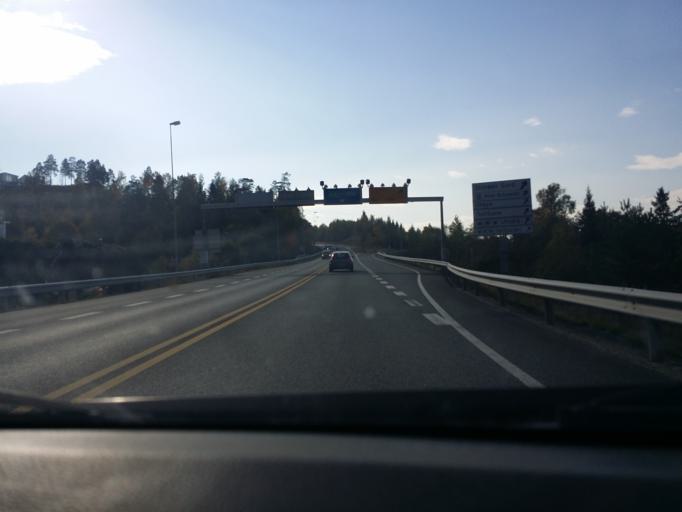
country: NO
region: Buskerud
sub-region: Hole
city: Vik
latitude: 60.0527
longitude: 10.2842
